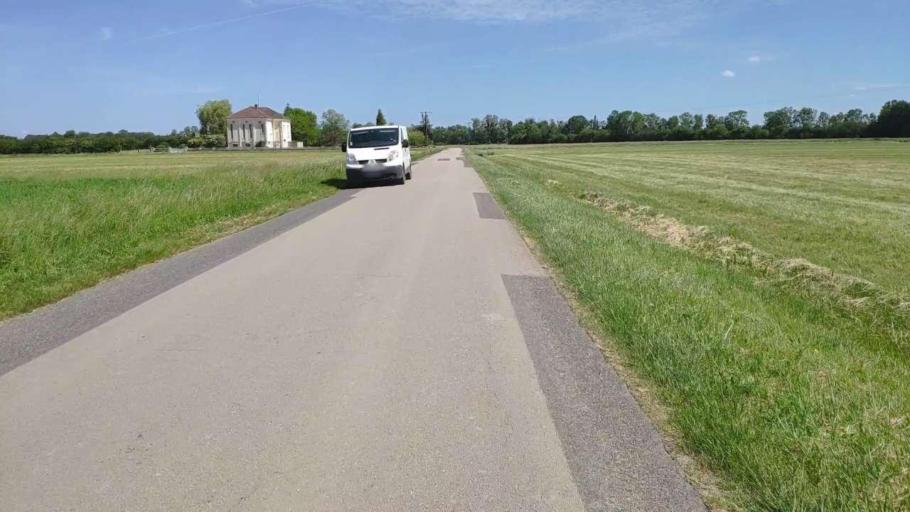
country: FR
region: Franche-Comte
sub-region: Departement du Jura
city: Bletterans
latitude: 46.7200
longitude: 5.4439
